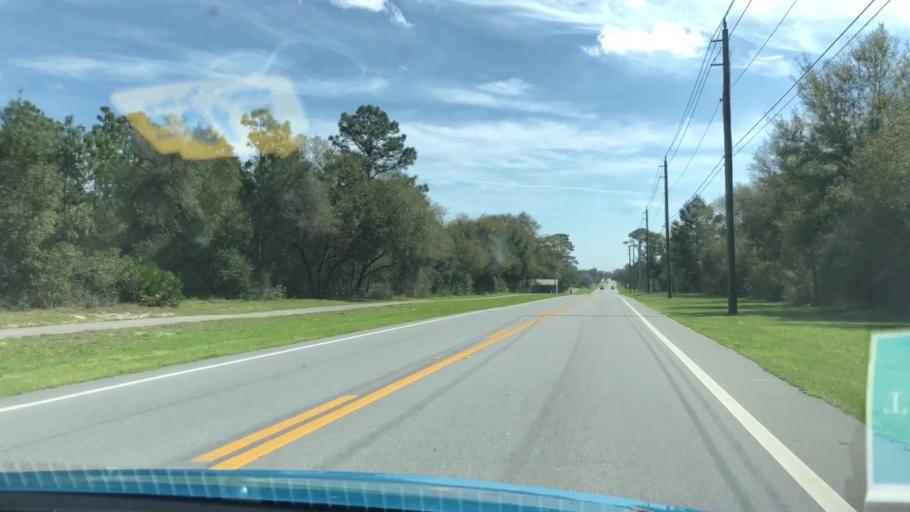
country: US
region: Florida
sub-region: Seminole County
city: Midway
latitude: 28.8557
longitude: -81.1841
